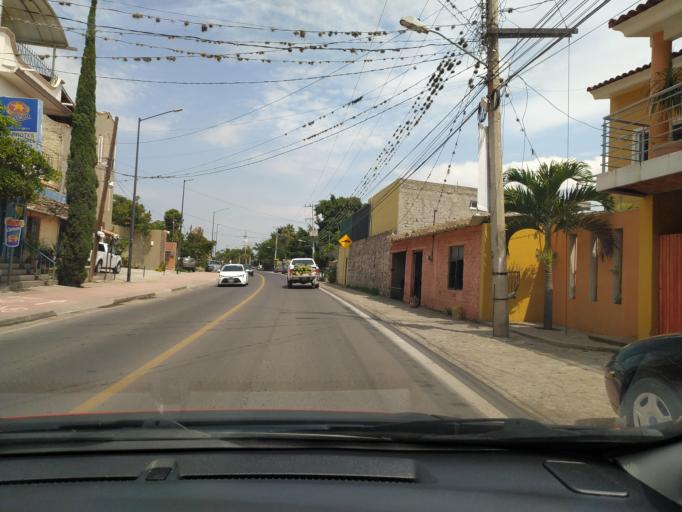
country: MX
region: Jalisco
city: San Juan Cosala
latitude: 20.2864
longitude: -103.3365
